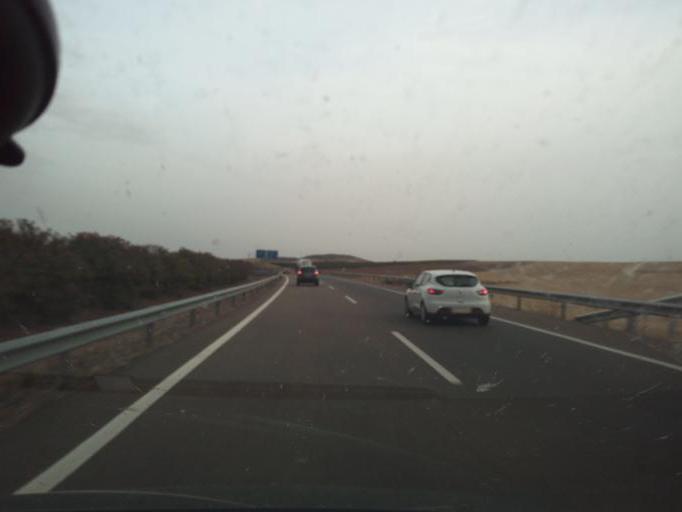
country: ES
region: Extremadura
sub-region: Provincia de Badajoz
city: Merida
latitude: 38.9472
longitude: -6.3204
